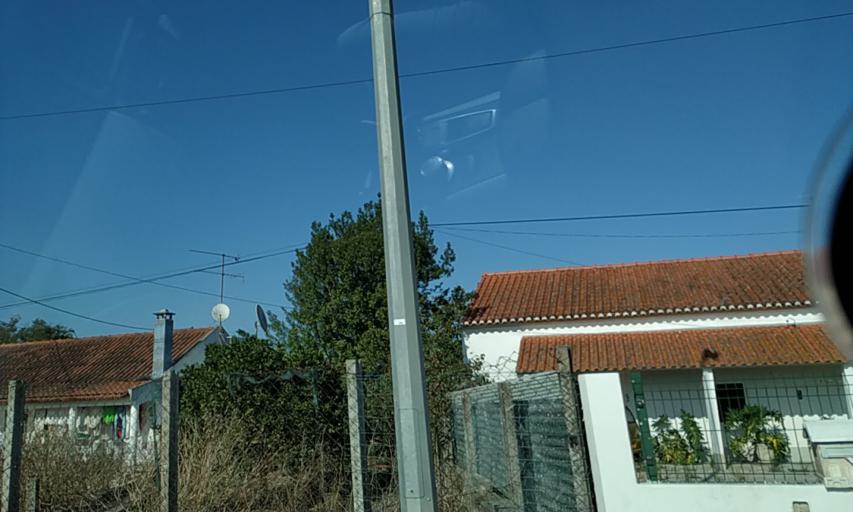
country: PT
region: Santarem
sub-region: Coruche
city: Coruche
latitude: 38.9682
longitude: -8.5358
